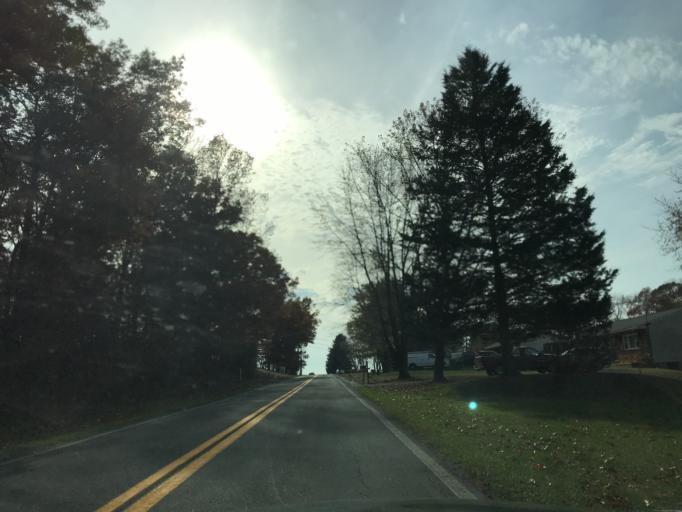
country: US
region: Maryland
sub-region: Carroll County
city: Eldersburg
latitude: 39.4603
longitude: -76.9094
